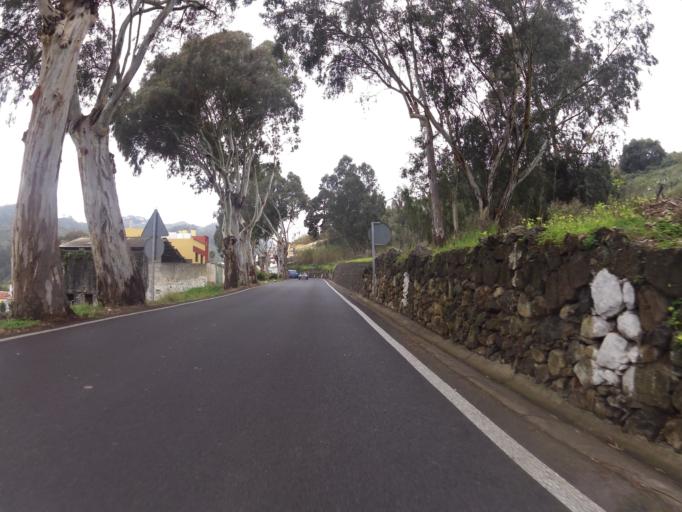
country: ES
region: Canary Islands
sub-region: Provincia de Las Palmas
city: Teror
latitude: 28.0663
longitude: -15.5385
